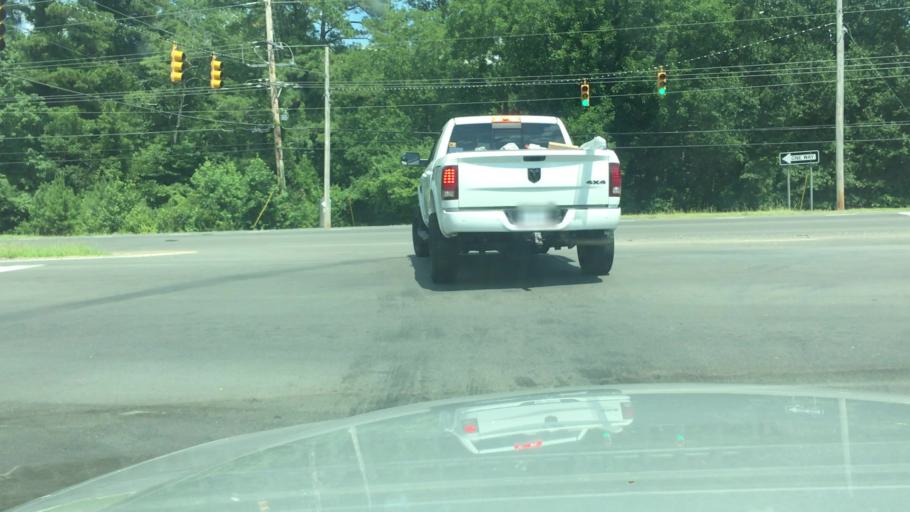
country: US
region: North Carolina
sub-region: Cumberland County
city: Vander
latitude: 34.9497
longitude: -78.8449
